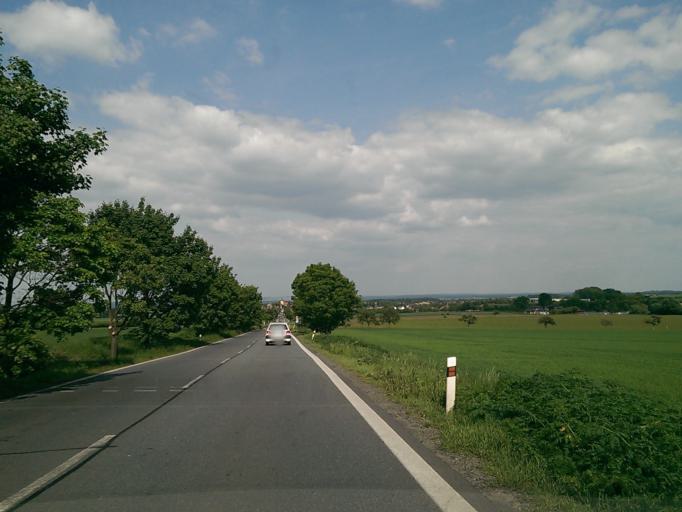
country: CZ
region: Central Bohemia
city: Zdiby
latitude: 50.1826
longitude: 14.4694
